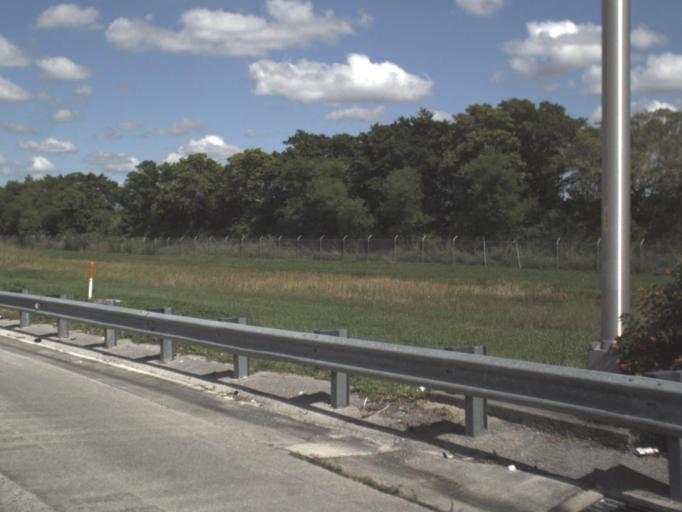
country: US
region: Florida
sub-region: Broward County
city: Coral Springs
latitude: 26.2880
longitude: -80.2970
